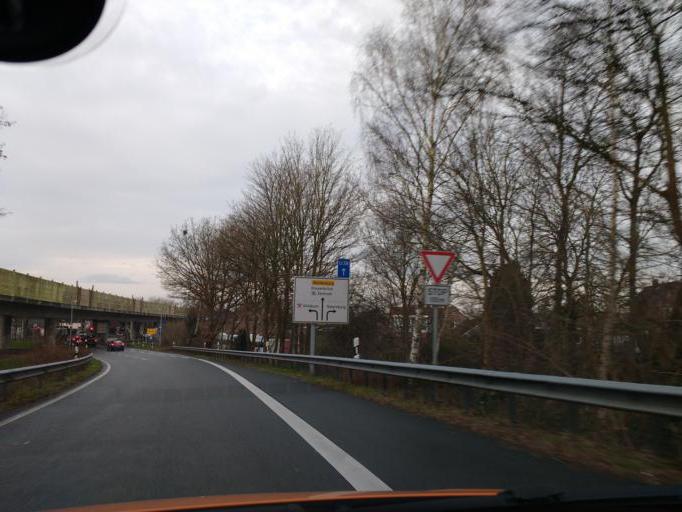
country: DE
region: Lower Saxony
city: Oldenburg
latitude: 53.1236
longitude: 8.2243
